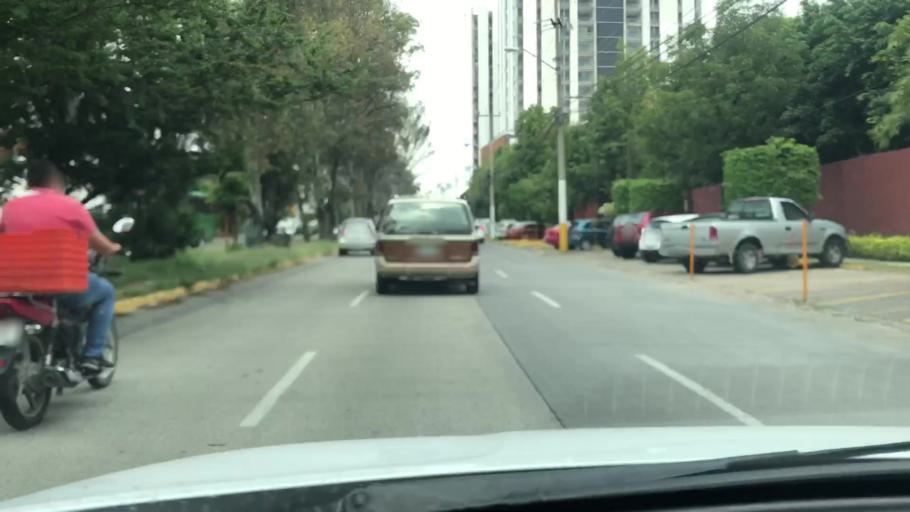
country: MX
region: Jalisco
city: Guadalajara
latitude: 20.6567
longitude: -103.4321
